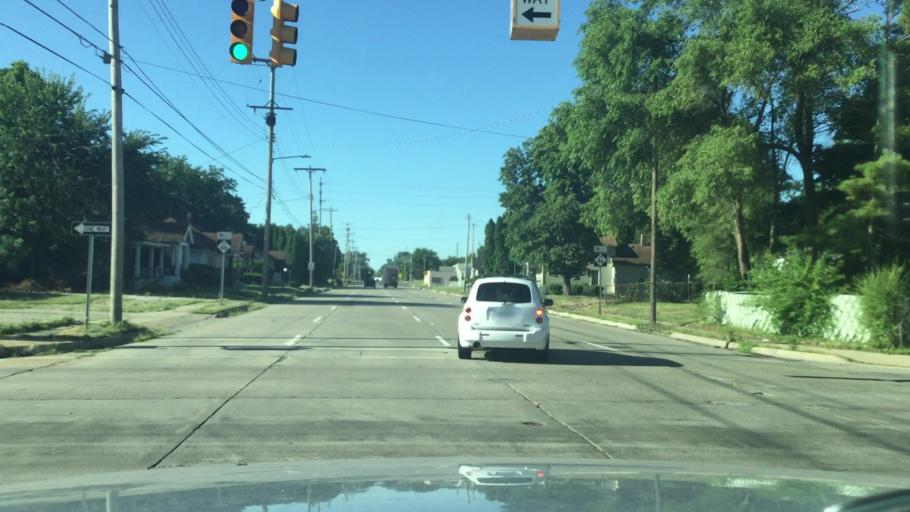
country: US
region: Michigan
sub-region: Saginaw County
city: Saginaw
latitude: 43.4149
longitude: -83.9359
